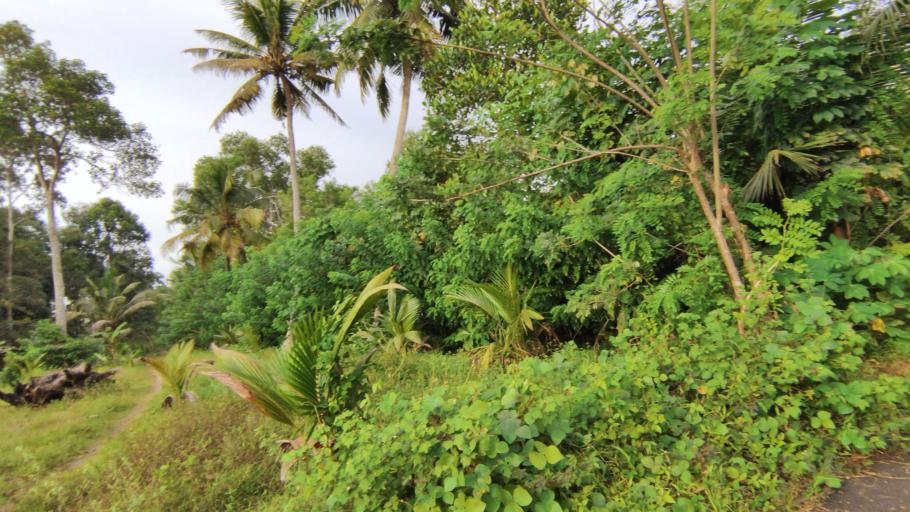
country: IN
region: Kerala
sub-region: Alappuzha
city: Shertallai
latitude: 9.6168
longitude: 76.3456
